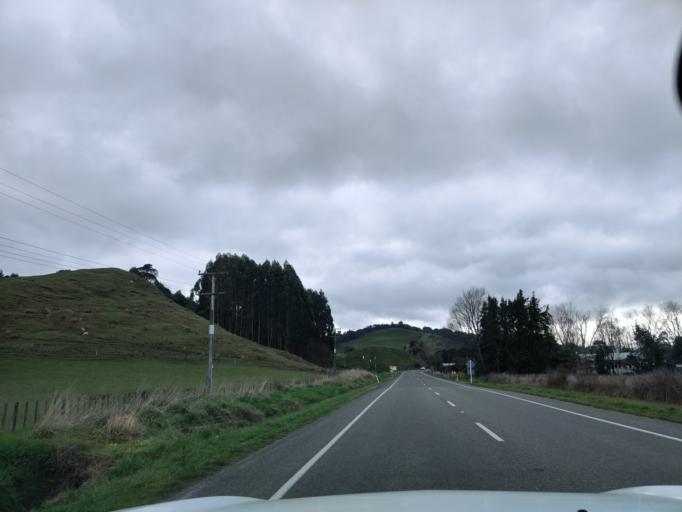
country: NZ
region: Manawatu-Wanganui
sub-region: Rangitikei District
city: Bulls
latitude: -39.9312
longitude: 175.5762
